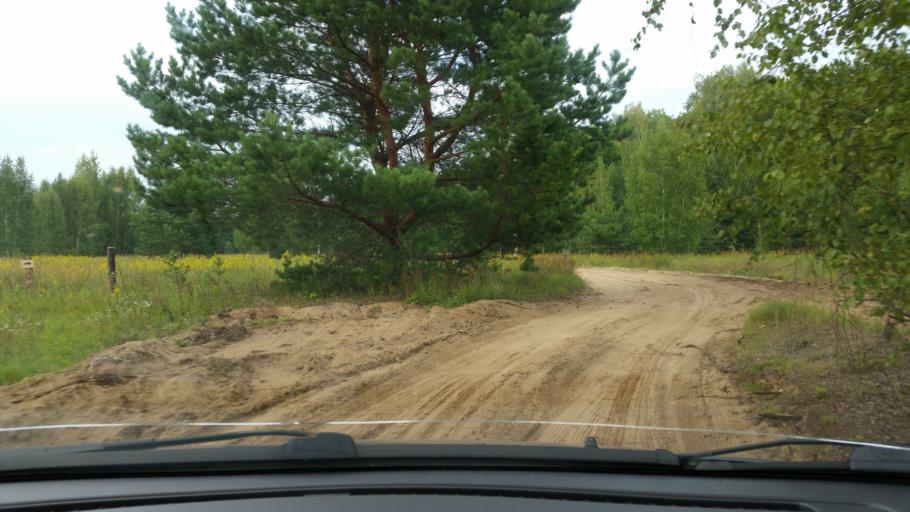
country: RU
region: Moskovskaya
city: Bol'shoye Gryzlovo
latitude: 54.8555
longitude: 37.7144
